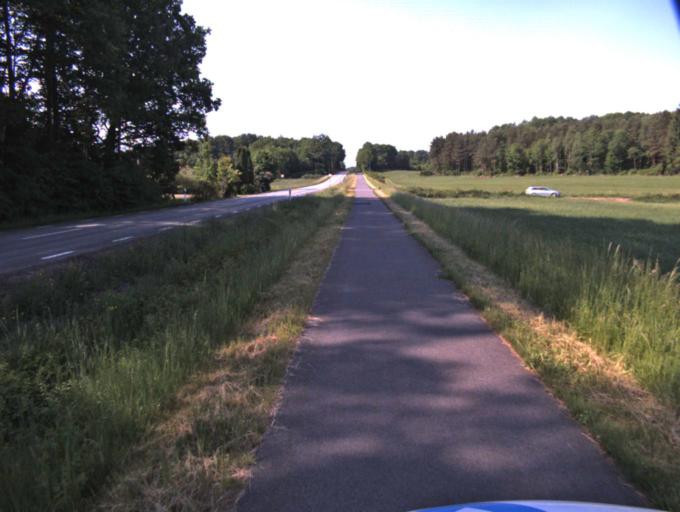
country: SE
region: Skane
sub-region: Kristianstads Kommun
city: Tollarp
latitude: 56.1597
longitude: 14.2721
